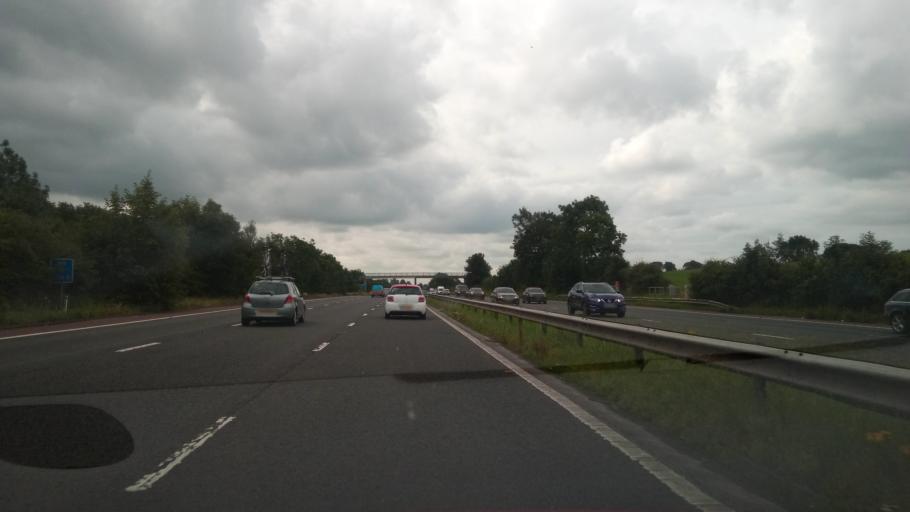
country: GB
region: England
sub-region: Lancashire
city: Galgate
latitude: 53.9955
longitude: -2.7806
